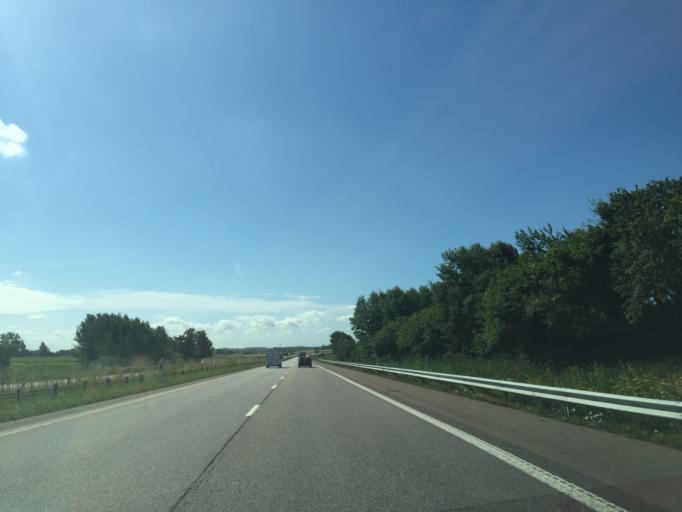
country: SE
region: Skane
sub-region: Angelholms Kommun
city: Strovelstorp
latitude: 56.1531
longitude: 12.8439
